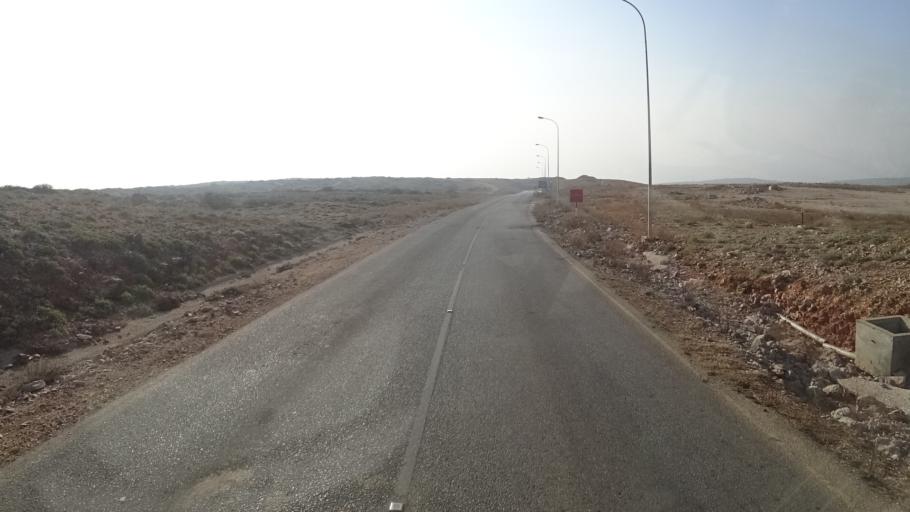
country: YE
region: Al Mahrah
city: Hawf
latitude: 16.7609
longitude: 53.2354
